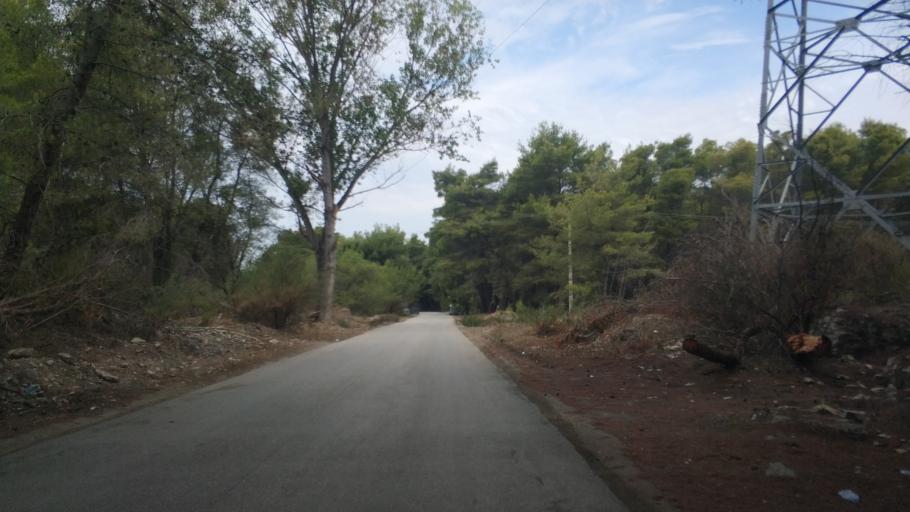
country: AL
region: Vlore
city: Vlore
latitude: 40.4878
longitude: 19.4429
